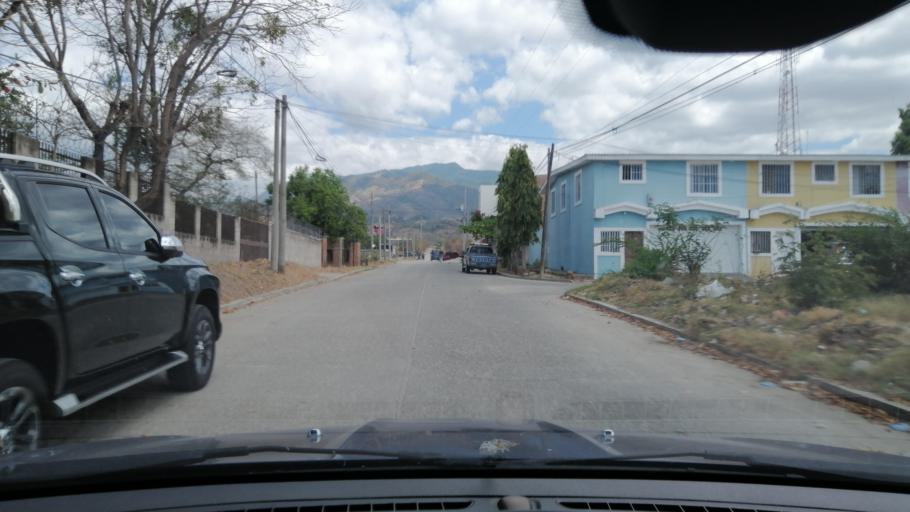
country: SV
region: Santa Ana
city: Metapan
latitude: 14.3347
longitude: -89.4406
